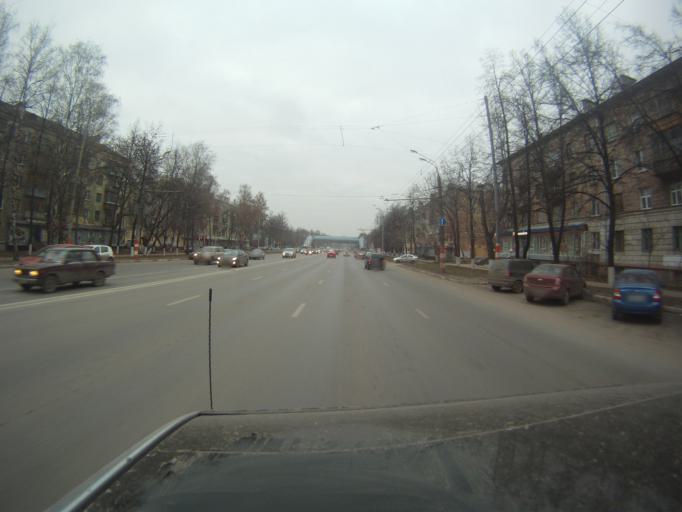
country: RU
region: Nizjnij Novgorod
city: Nizhniy Novgorod
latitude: 56.3017
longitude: 43.9842
